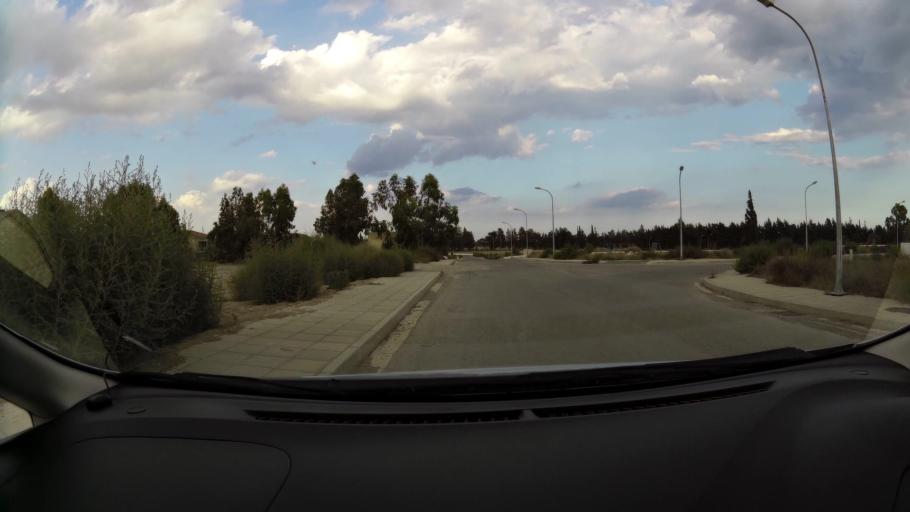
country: CY
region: Larnaka
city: Meneou
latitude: 34.8593
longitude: 33.5925
